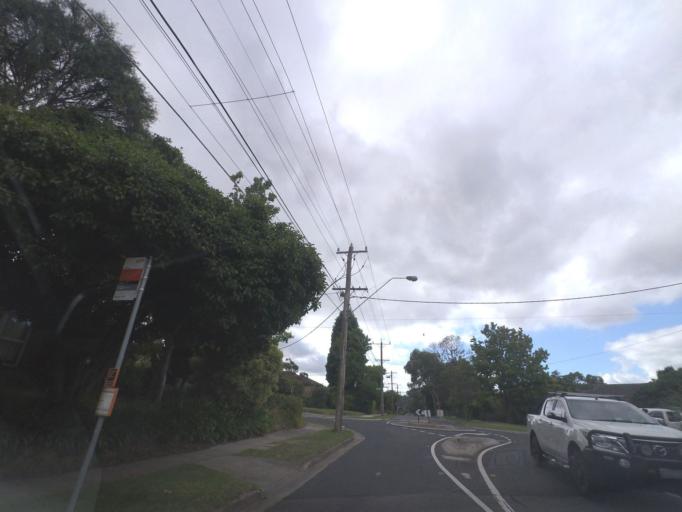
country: AU
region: Victoria
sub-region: Whitehorse
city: Vermont
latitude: -37.8309
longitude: 145.2088
